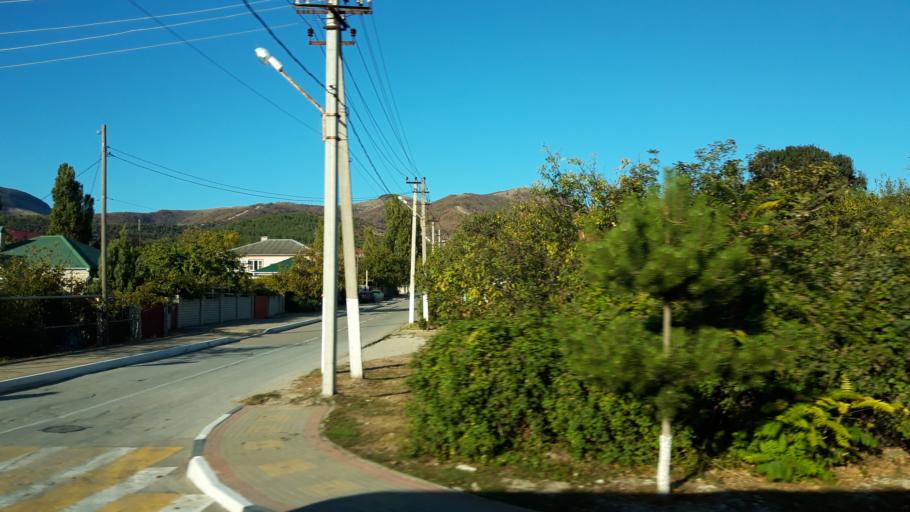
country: RU
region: Krasnodarskiy
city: Kabardinka
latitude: 44.6475
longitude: 37.9512
